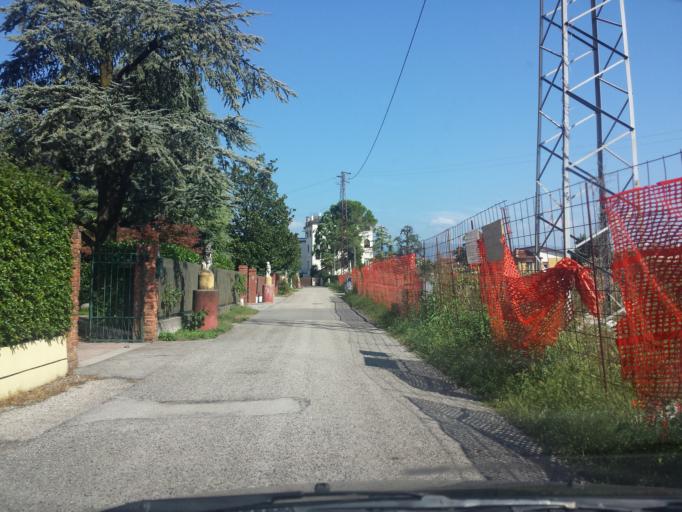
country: IT
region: Veneto
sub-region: Provincia di Vicenza
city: Sandrigo
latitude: 45.6649
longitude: 11.5956
